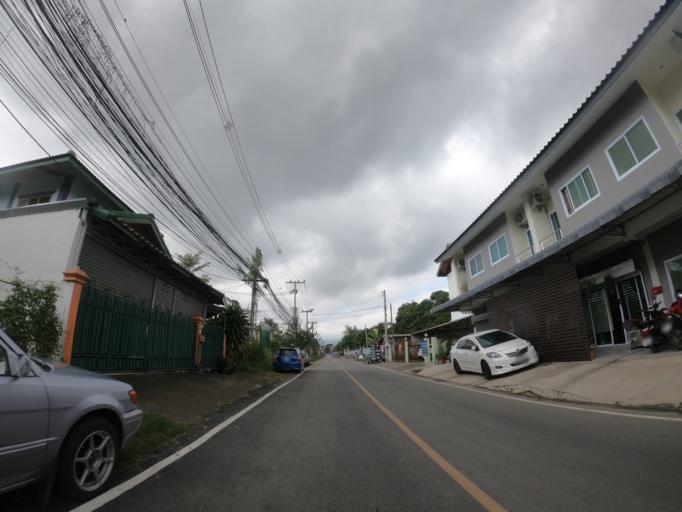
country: TH
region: Chiang Mai
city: Chiang Mai
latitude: 18.7508
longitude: 98.9747
